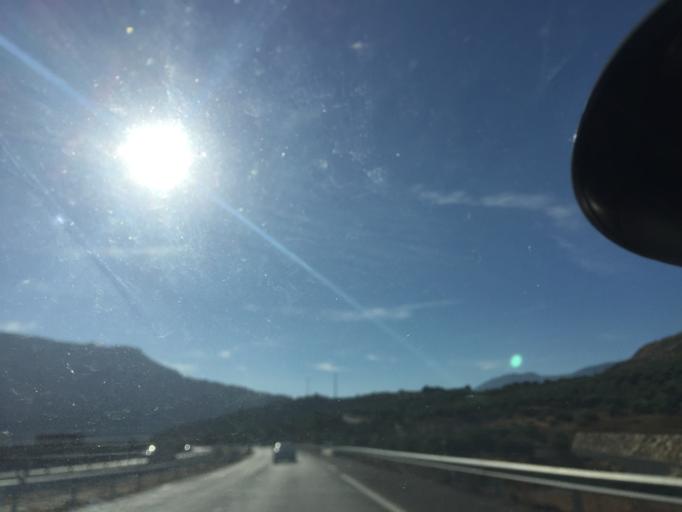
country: ES
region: Andalusia
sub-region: Provincia de Jaen
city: La Guardia de Jaen
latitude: 37.7551
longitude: -3.7004
